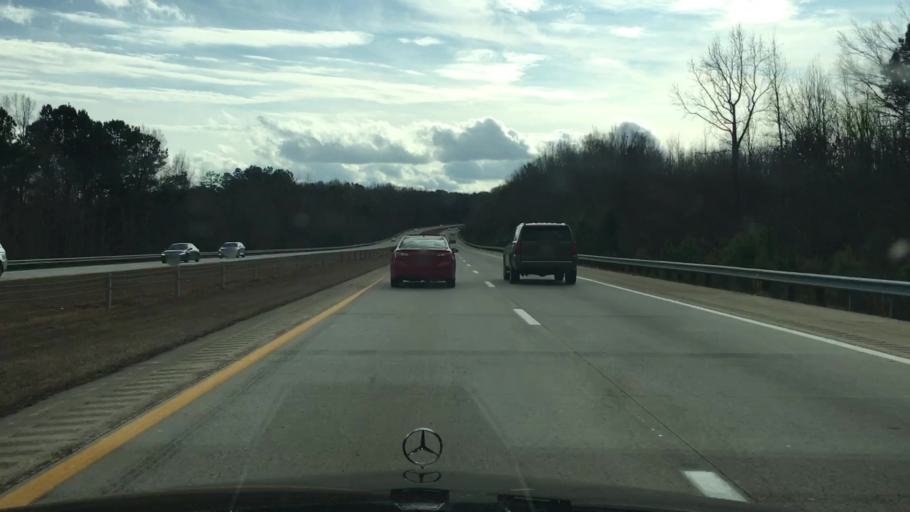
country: US
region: North Carolina
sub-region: Johnston County
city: Clayton
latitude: 35.5659
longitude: -78.5761
